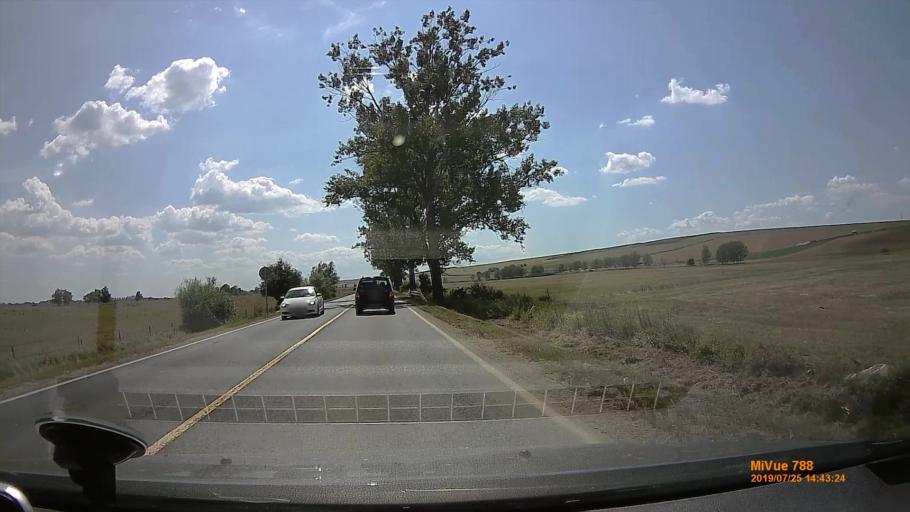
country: HU
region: Borsod-Abauj-Zemplen
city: Halmaj
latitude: 48.2734
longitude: 21.0117
